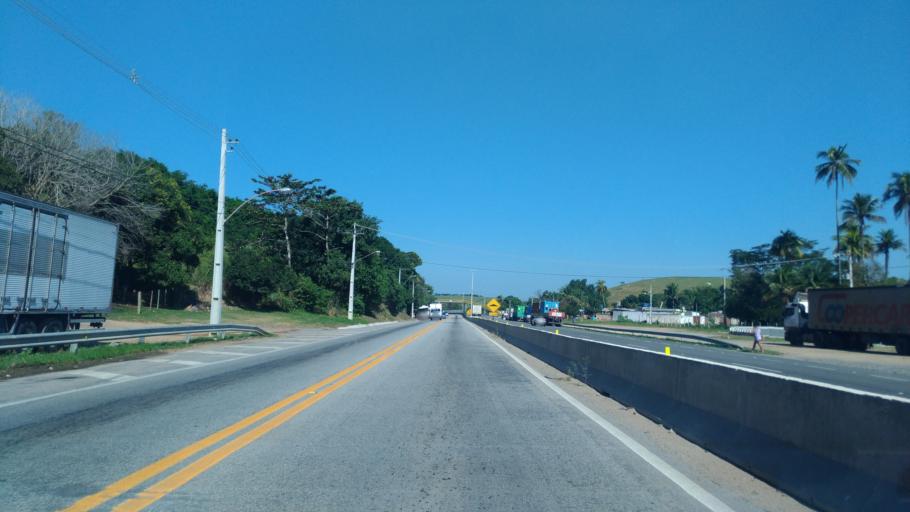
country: BR
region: Rio de Janeiro
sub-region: Macae
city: Macae
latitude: -22.0302
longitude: -41.6930
